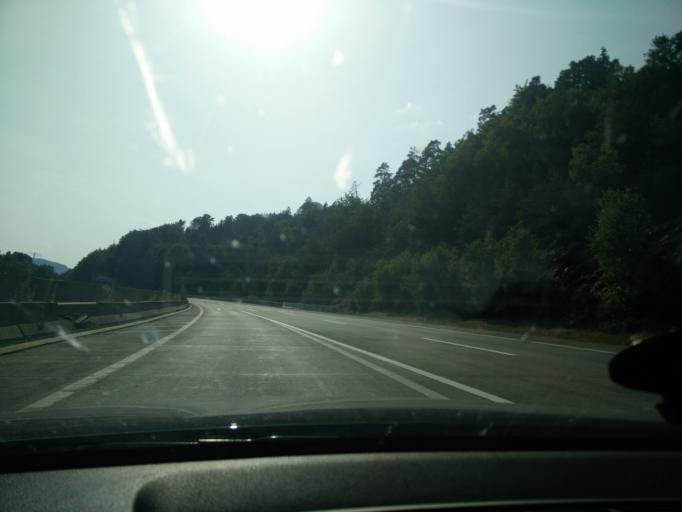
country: AT
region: Carinthia
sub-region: Politischer Bezirk Klagenfurt Land
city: Keutschach am See
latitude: 46.6310
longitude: 14.2350
